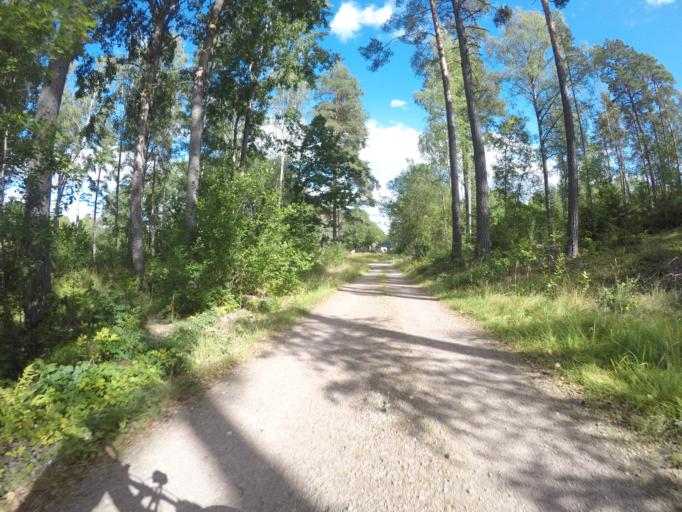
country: SE
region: Vaestmanland
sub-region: Hallstahammars Kommun
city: Kolback
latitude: 59.4971
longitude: 16.2051
